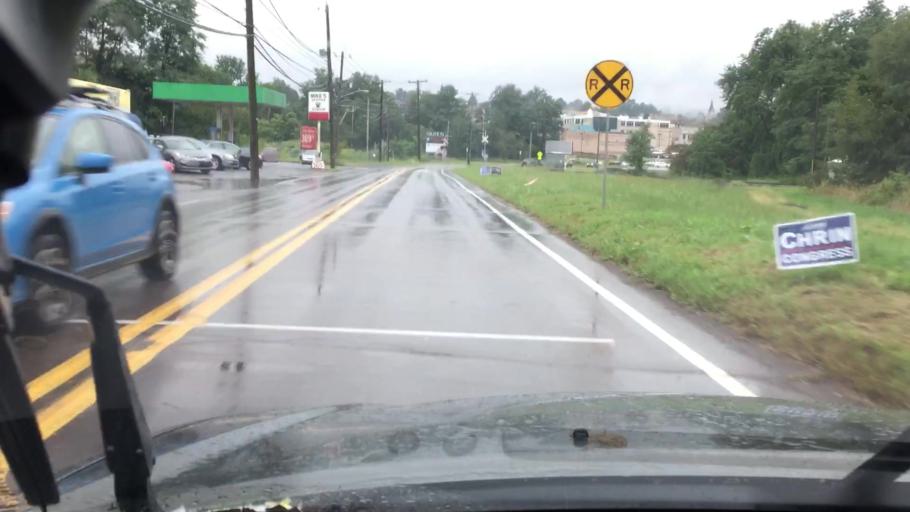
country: US
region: Pennsylvania
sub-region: Luzerne County
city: Nanticoke
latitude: 41.2101
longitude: -76.0042
